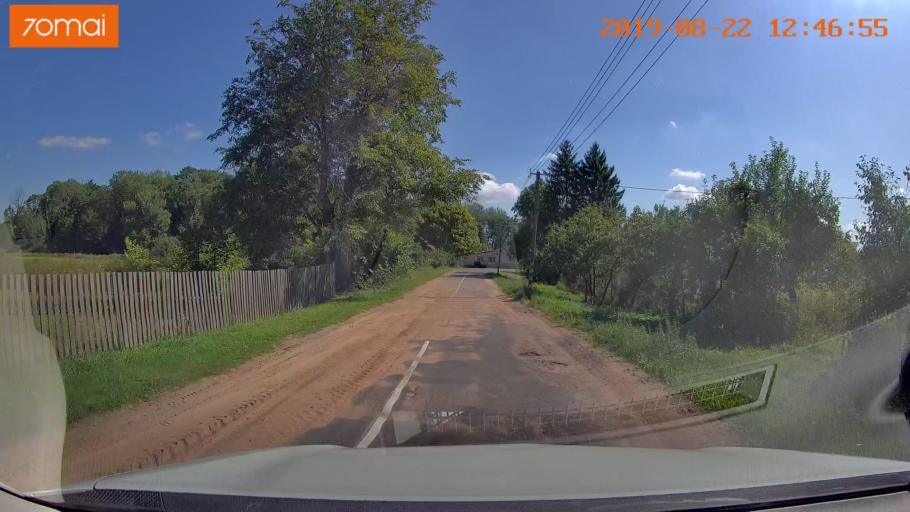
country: BY
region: Minsk
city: Prawdzinski
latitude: 53.4579
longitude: 27.6352
